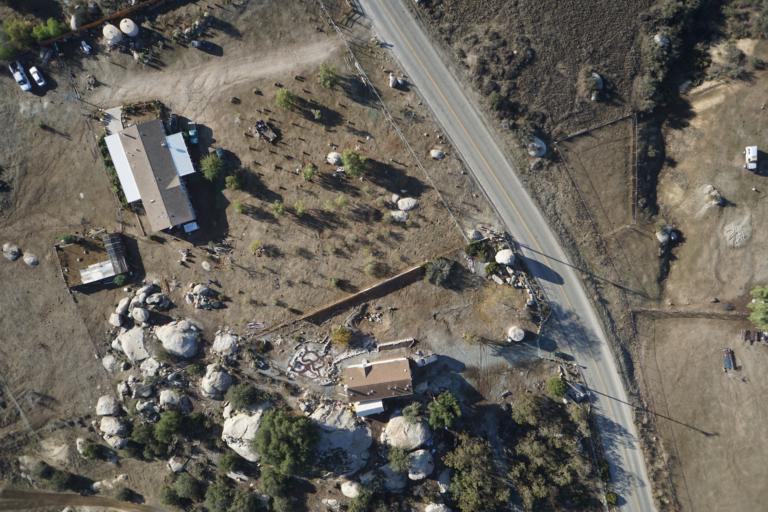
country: US
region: California
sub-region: Riverside County
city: East Hemet
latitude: 33.6222
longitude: -116.9005
